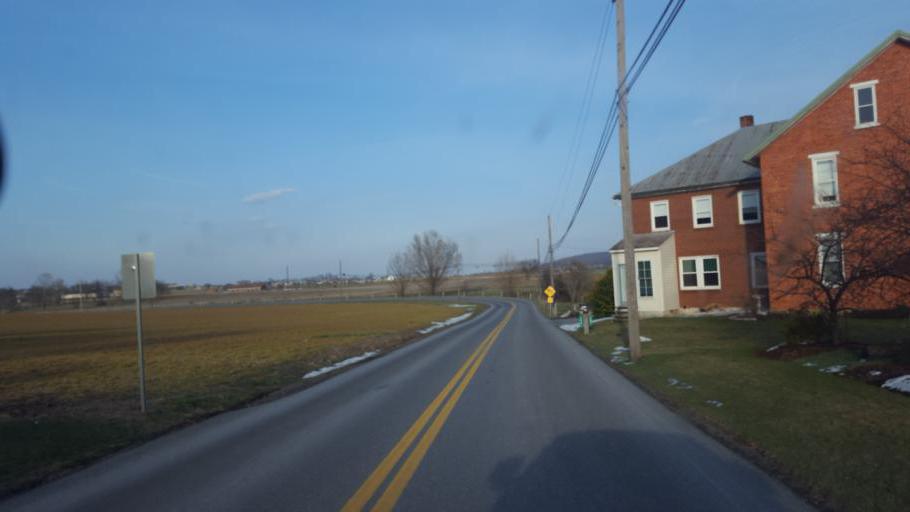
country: US
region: Pennsylvania
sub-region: Lancaster County
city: New Holland
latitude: 40.0881
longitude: -76.0854
